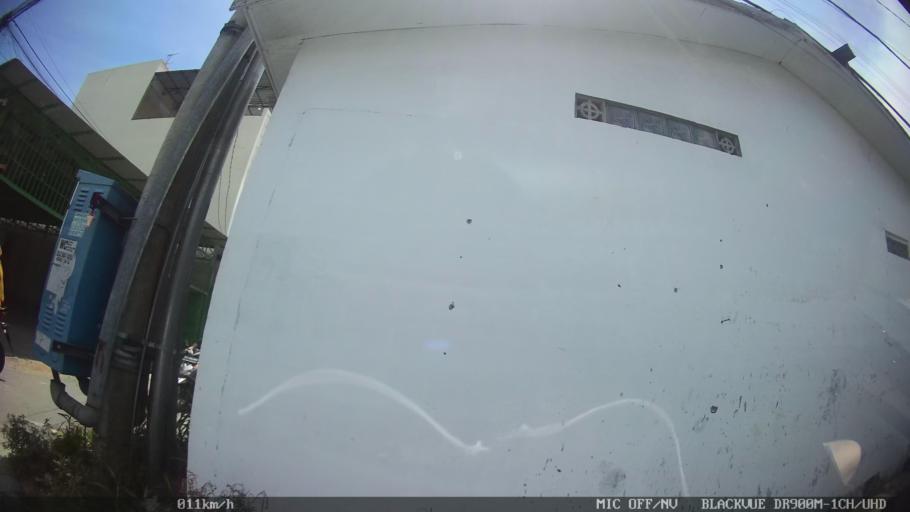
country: ID
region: North Sumatra
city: Binjai
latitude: 3.6127
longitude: 98.4923
